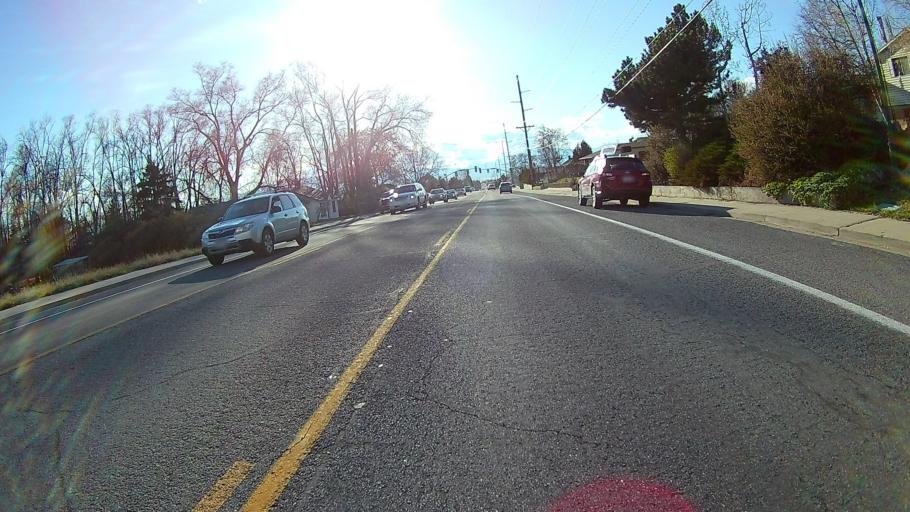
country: US
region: Utah
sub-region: Utah County
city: Orem
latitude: 40.3266
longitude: -111.6849
